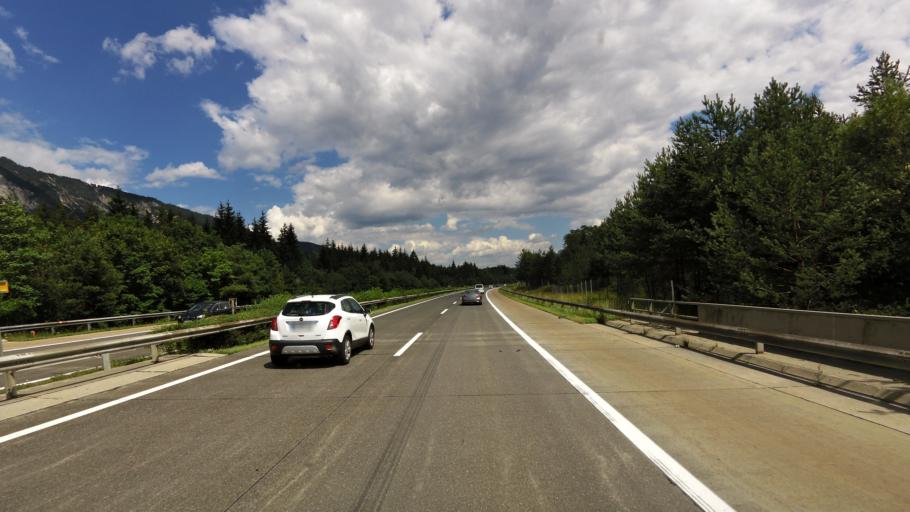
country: AT
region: Carinthia
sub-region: Politischer Bezirk Villach Land
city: Arnoldstein
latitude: 46.5683
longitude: 13.7238
